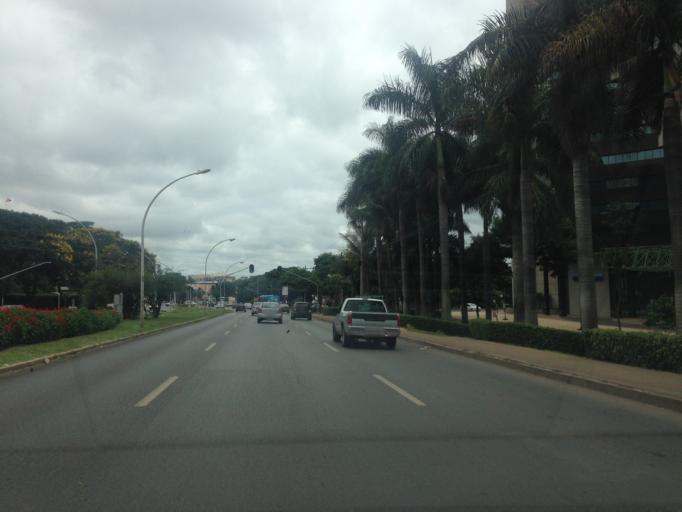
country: BR
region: Federal District
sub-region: Brasilia
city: Brasilia
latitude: -15.7870
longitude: -47.8880
